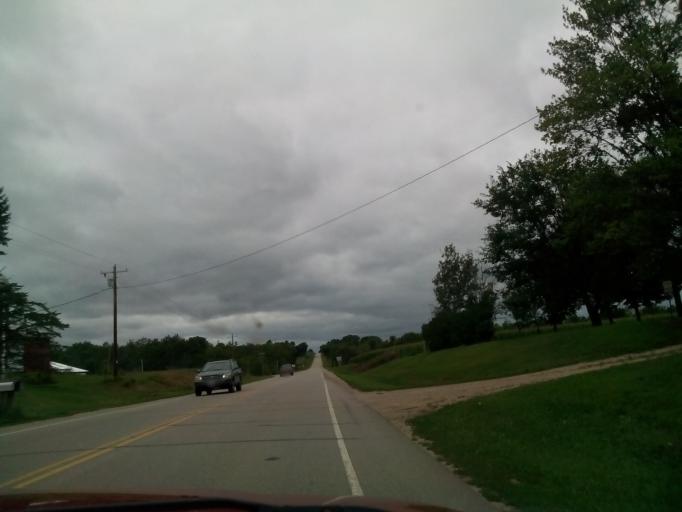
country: US
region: Wisconsin
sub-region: Menominee County
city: Legend Lake
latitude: 44.9935
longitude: -88.4459
